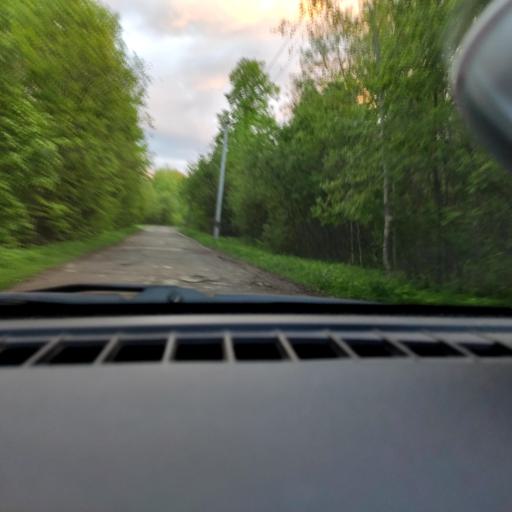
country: RU
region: Perm
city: Perm
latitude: 58.0827
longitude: 56.3849
